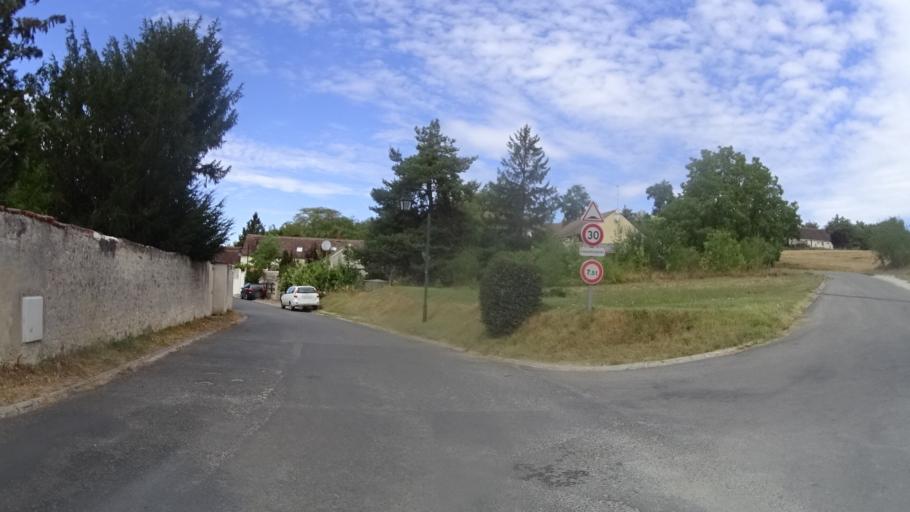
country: FR
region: Centre
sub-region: Departement du Loiret
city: Malesherbes
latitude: 48.2612
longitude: 2.4280
